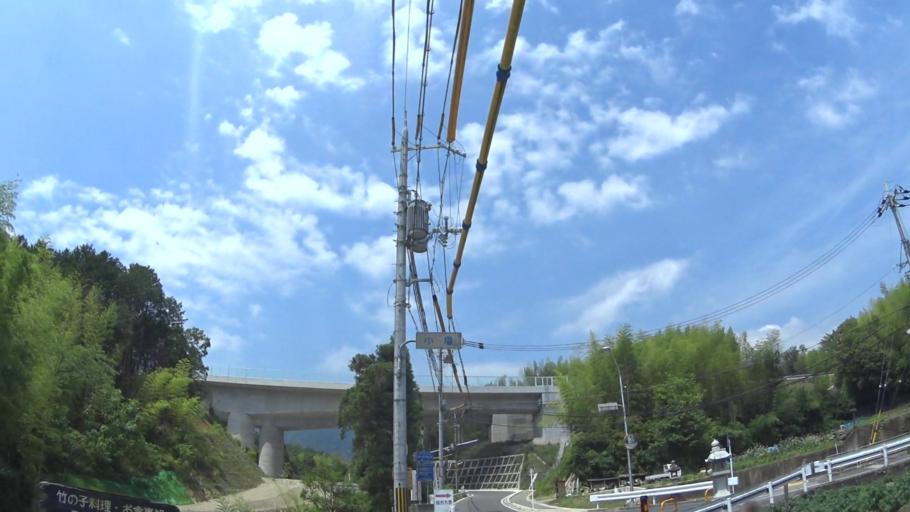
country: JP
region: Kyoto
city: Muko
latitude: 34.9466
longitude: 135.6655
